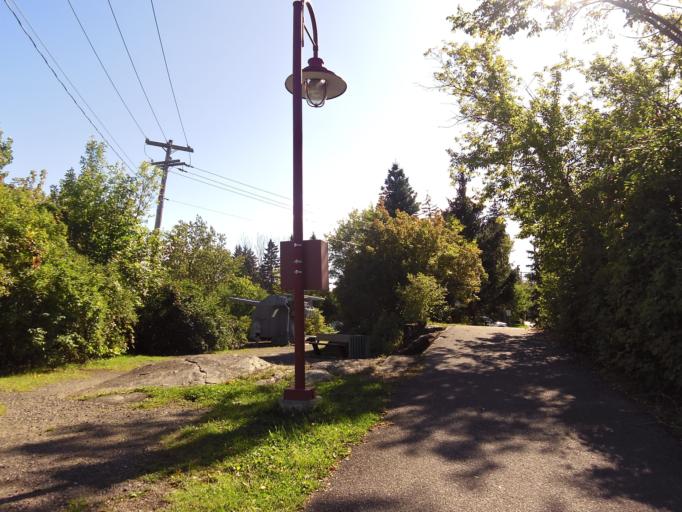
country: CA
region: Ontario
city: Clarence-Rockland
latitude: 45.5863
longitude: -75.4201
